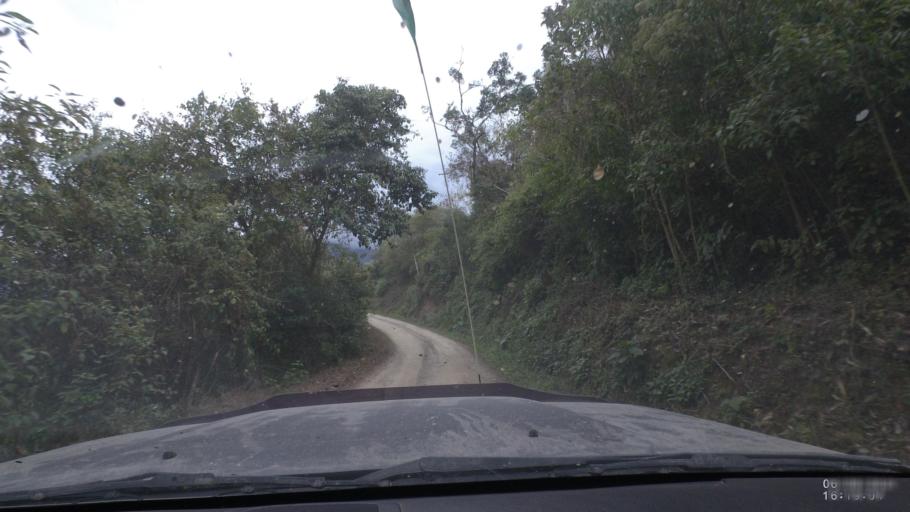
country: BO
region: La Paz
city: Quime
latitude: -16.5503
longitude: -66.7443
